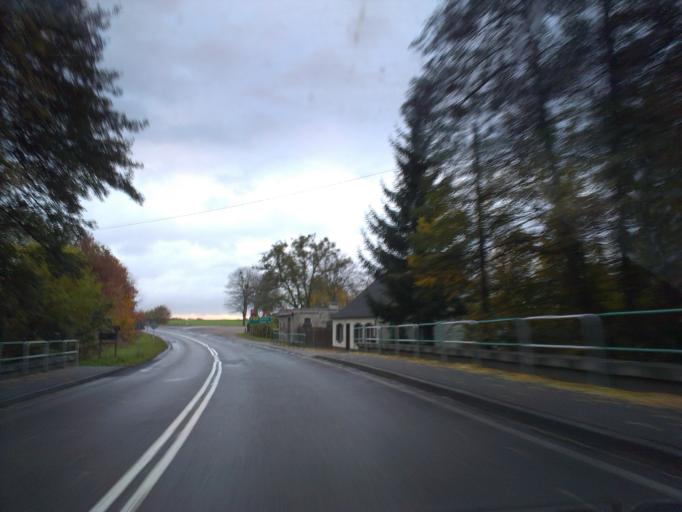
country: PL
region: Kujawsko-Pomorskie
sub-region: Powiat tucholski
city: Cekcyn
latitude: 53.5184
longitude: 17.9528
